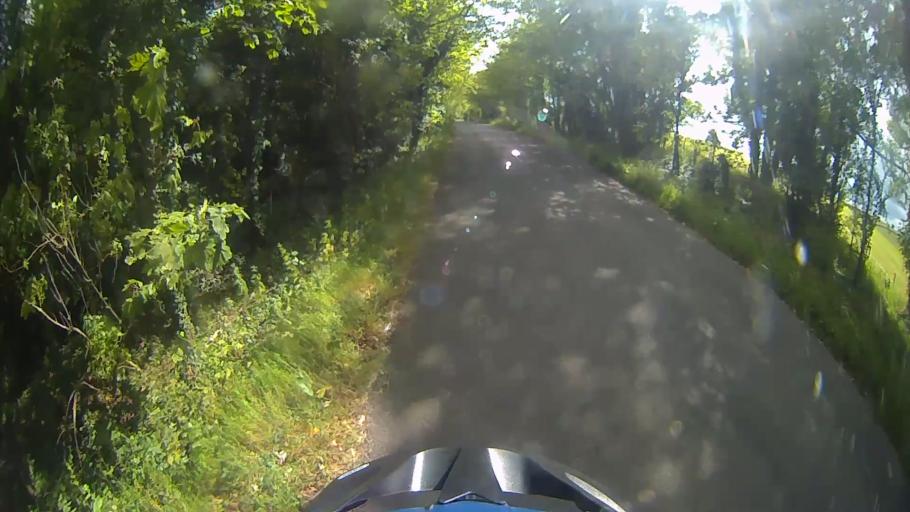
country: GB
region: England
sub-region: Oxfordshire
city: Stanford in the Vale
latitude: 51.5806
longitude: -1.5342
